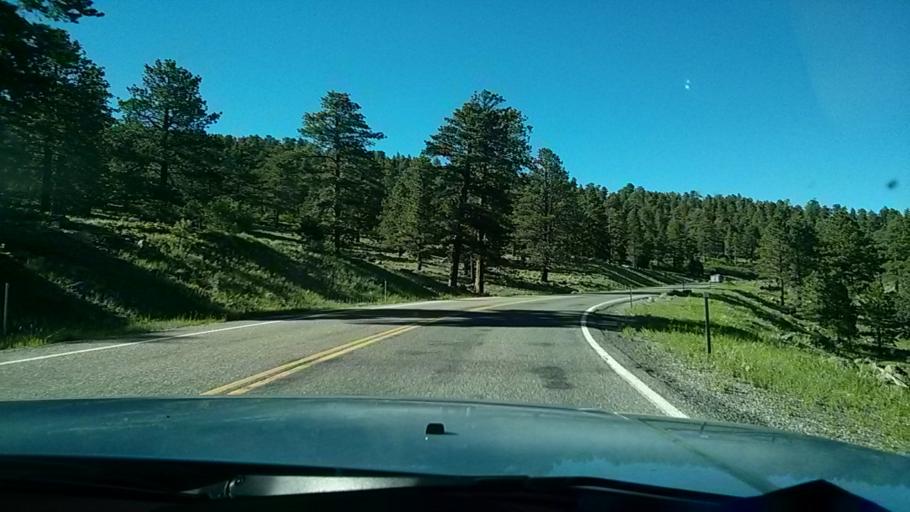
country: US
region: Utah
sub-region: Wayne County
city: Loa
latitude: 38.1138
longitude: -111.3298
